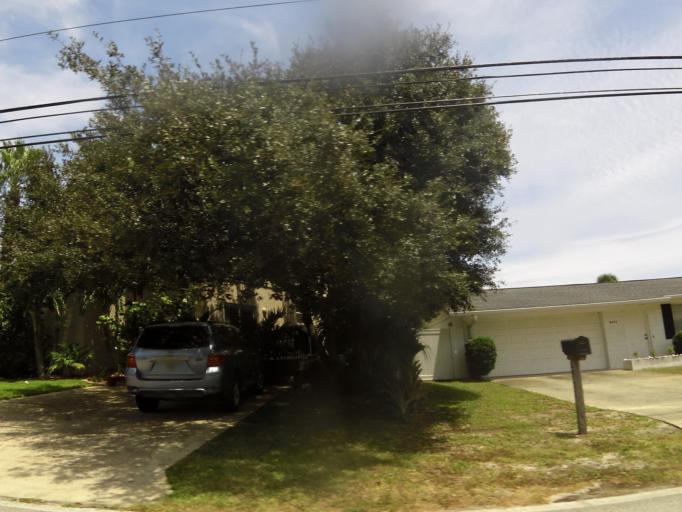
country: US
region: Florida
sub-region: Volusia County
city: Ponce Inlet
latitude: 29.0967
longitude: -80.9394
